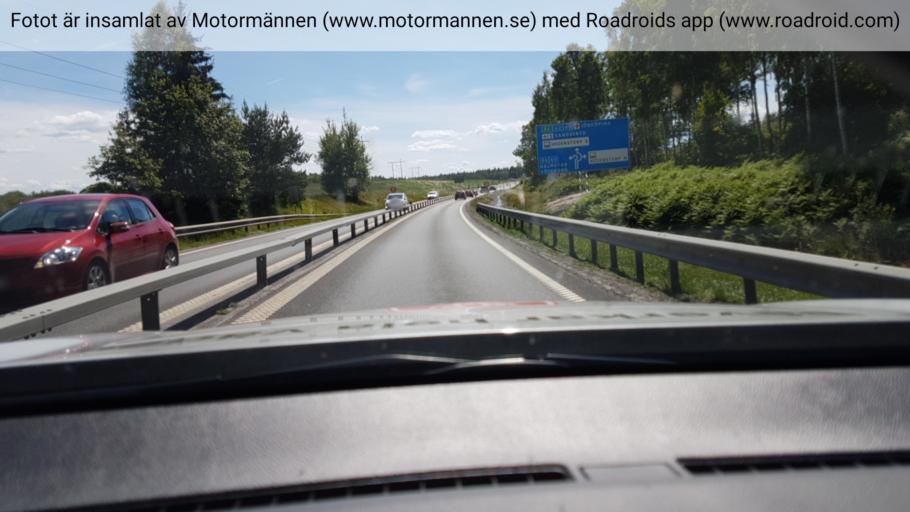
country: SE
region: Joenkoeping
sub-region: Jonkopings Kommun
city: Jonkoping
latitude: 57.7700
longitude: 14.1045
